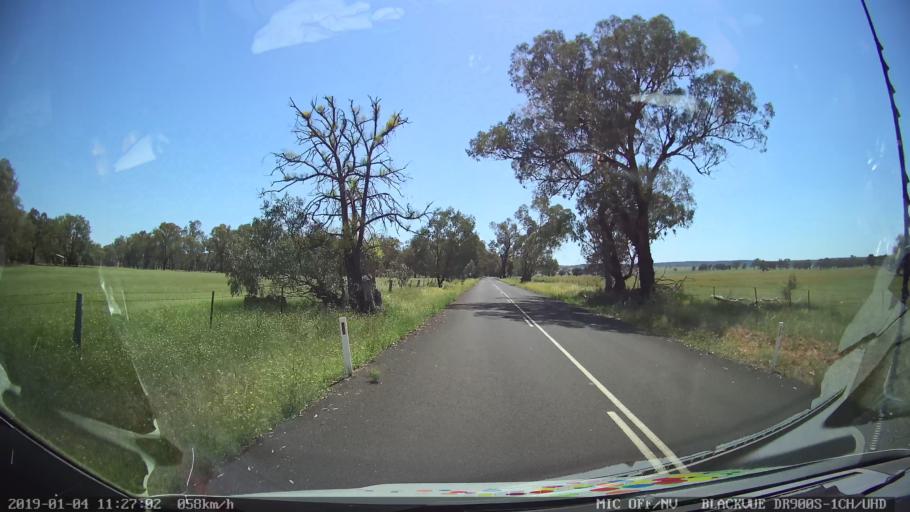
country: AU
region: New South Wales
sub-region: Cabonne
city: Molong
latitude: -33.1114
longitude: 148.7583
